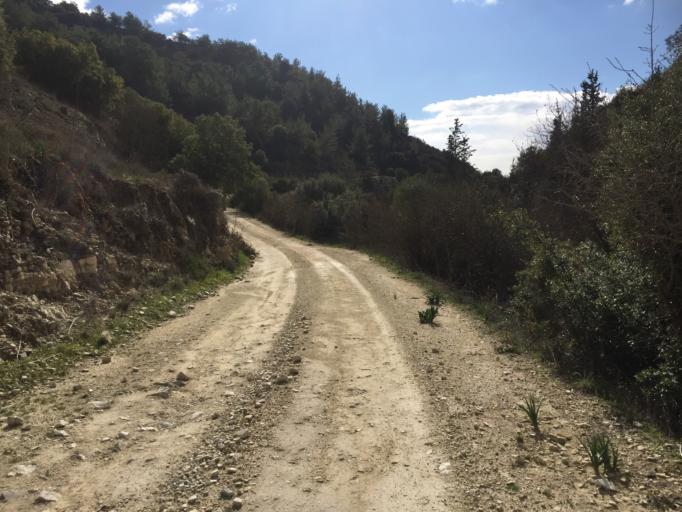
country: CY
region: Pafos
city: Mesogi
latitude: 34.8307
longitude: 32.5183
